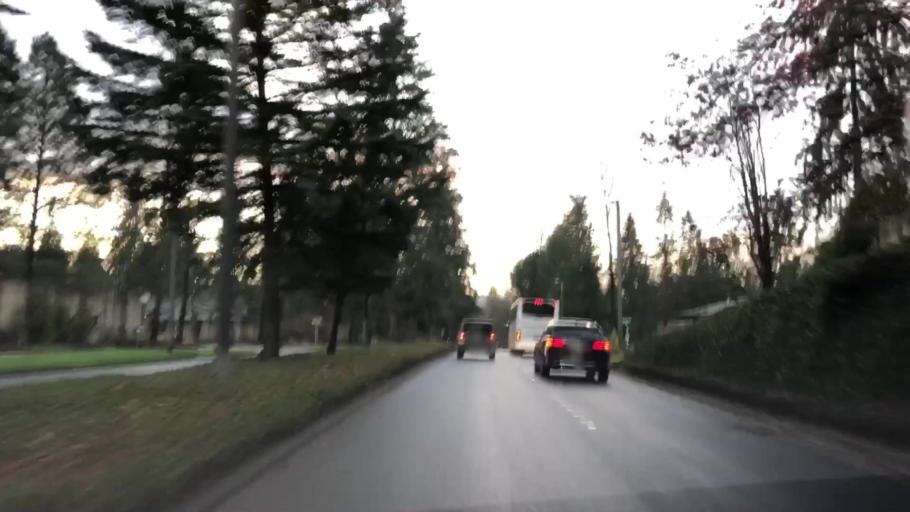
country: US
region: Washington
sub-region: King County
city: Eastgate
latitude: 47.6236
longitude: -122.1432
